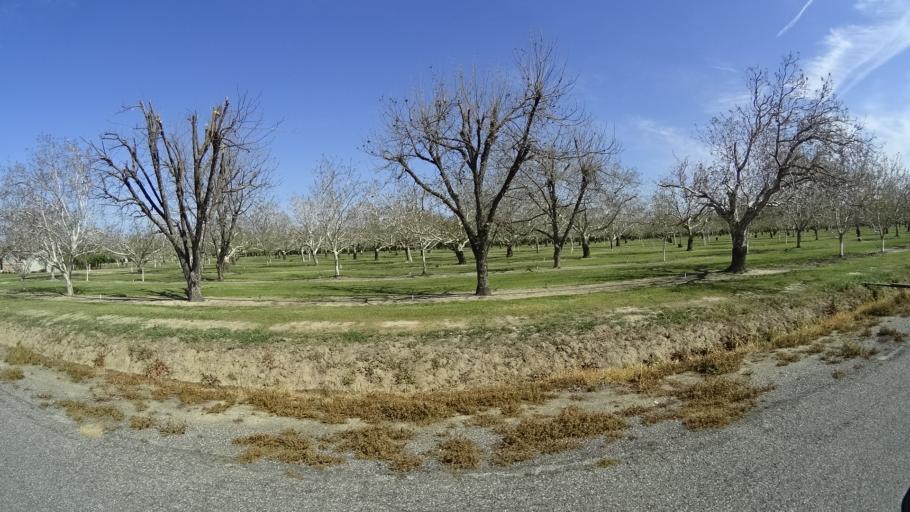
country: US
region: California
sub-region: Glenn County
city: Hamilton City
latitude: 39.6160
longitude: -122.0122
